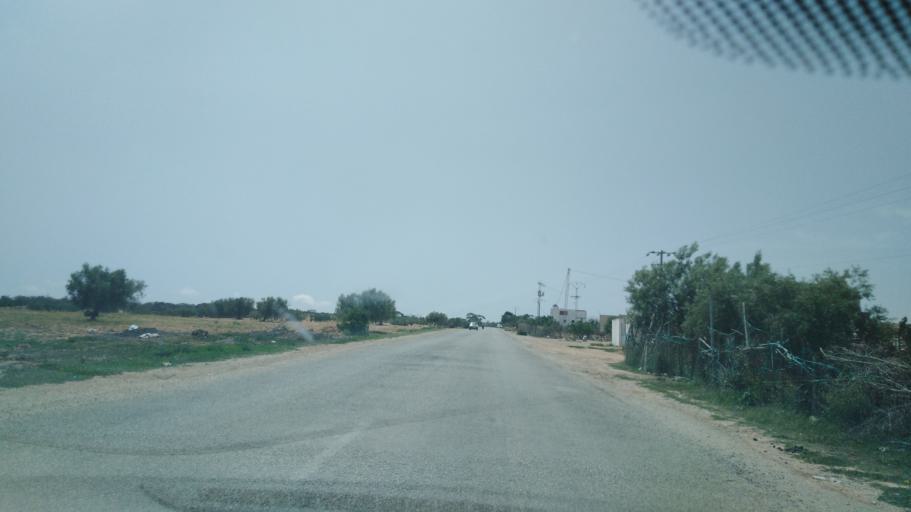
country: TN
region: Safaqis
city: Sfax
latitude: 34.7283
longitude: 10.5768
